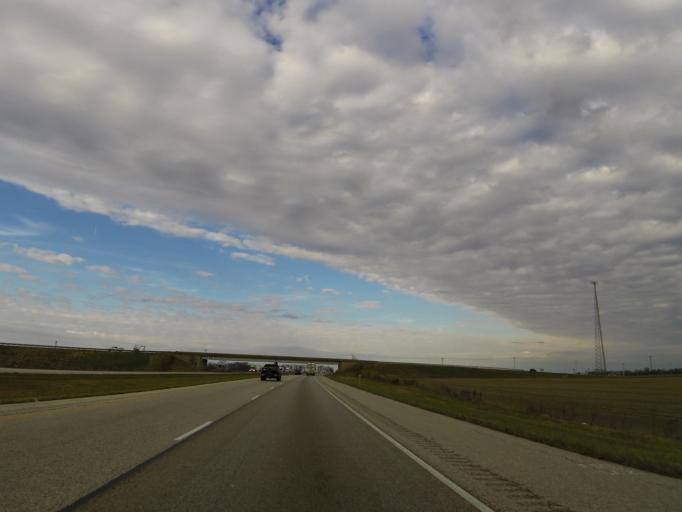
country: US
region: Illinois
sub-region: Washington County
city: Nashville
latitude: 38.4129
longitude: -89.4337
